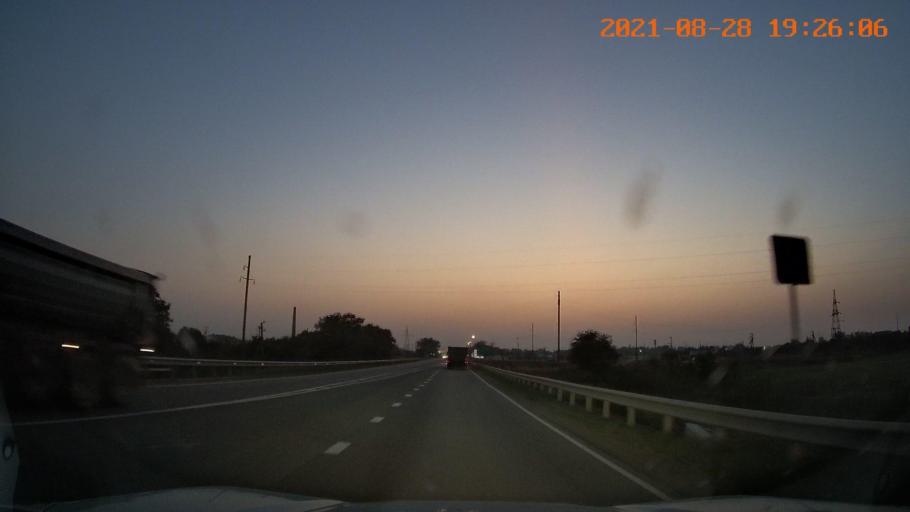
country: RU
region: Adygeya
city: Ponezhukay
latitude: 44.8781
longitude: 39.3997
